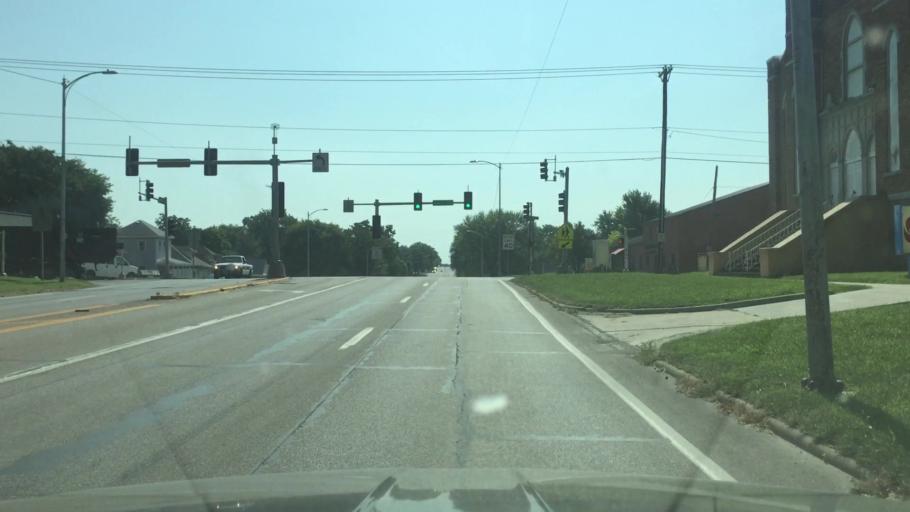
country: US
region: Missouri
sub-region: Pettis County
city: Sedalia
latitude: 38.7036
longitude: -93.2140
